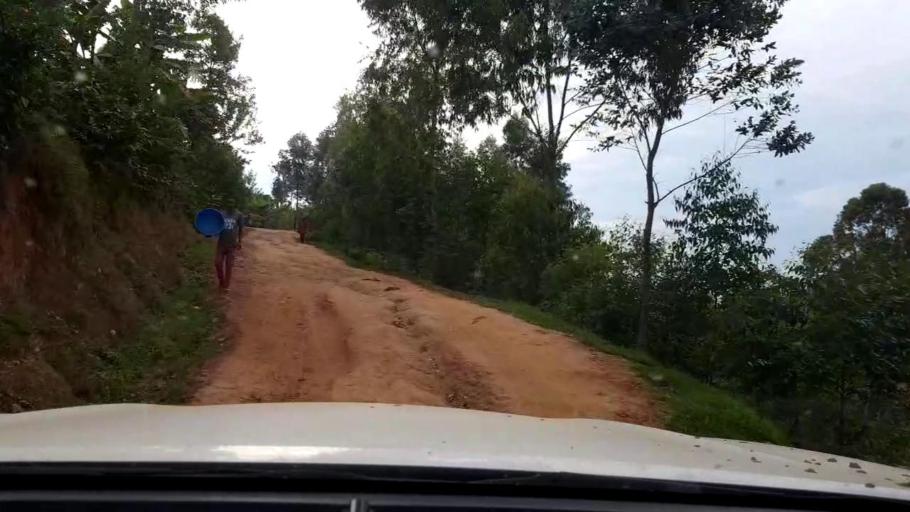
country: RW
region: Western Province
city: Kibuye
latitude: -2.0027
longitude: 29.3735
